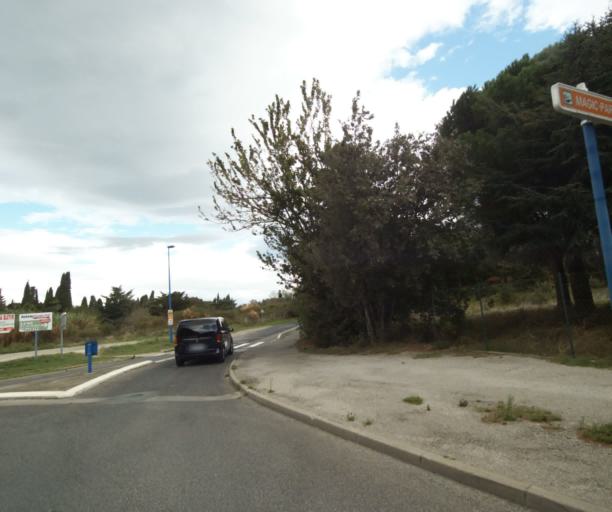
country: FR
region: Languedoc-Roussillon
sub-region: Departement des Pyrenees-Orientales
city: Argelers
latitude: 42.5538
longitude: 3.0268
